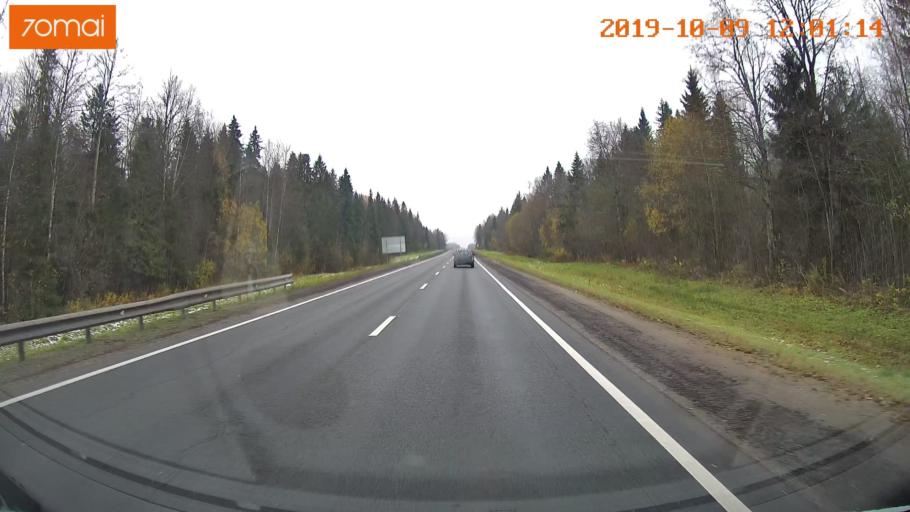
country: RU
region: Vologda
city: Gryazovets
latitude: 58.6903
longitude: 40.3025
